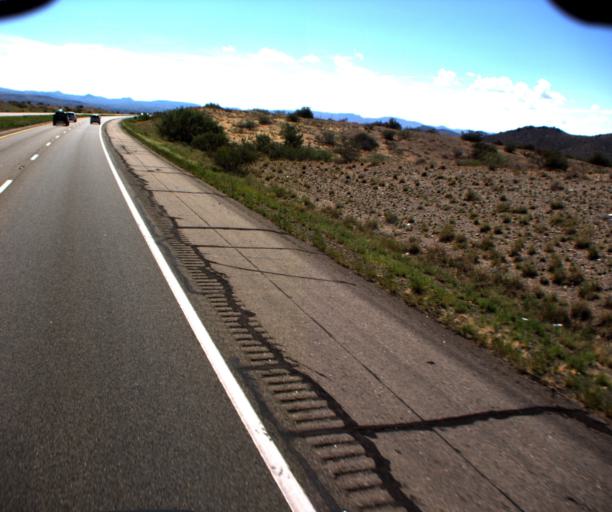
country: US
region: Arizona
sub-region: Yavapai County
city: Spring Valley
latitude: 34.3480
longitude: -112.1491
